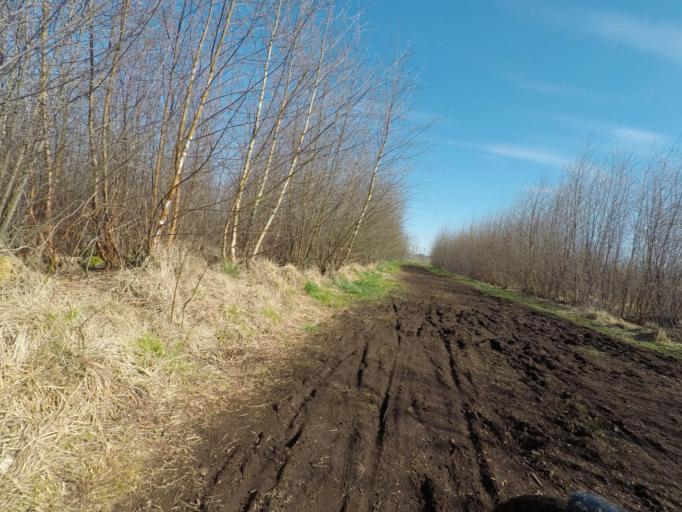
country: DE
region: Hamburg
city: Langenhorn
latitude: 53.6513
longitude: 9.9745
